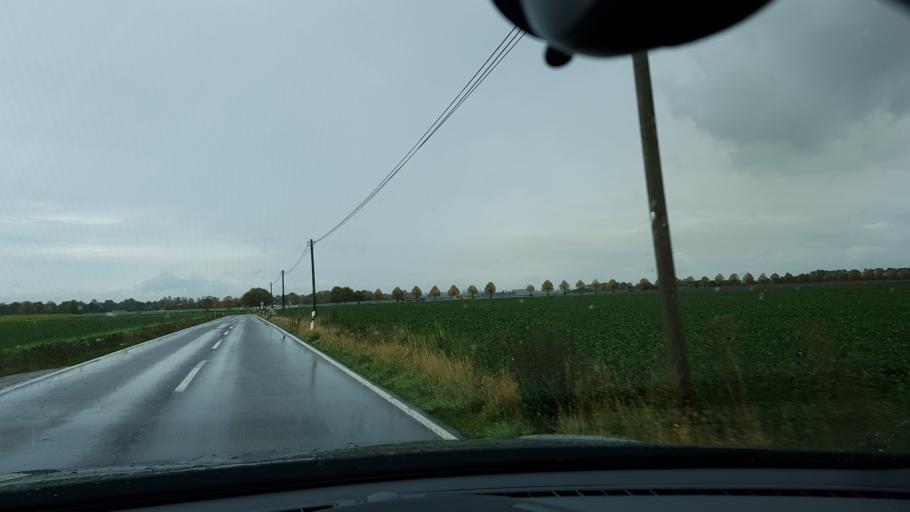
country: DE
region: North Rhine-Westphalia
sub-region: Regierungsbezirk Dusseldorf
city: Rommerskirchen
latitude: 51.0549
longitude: 6.6404
